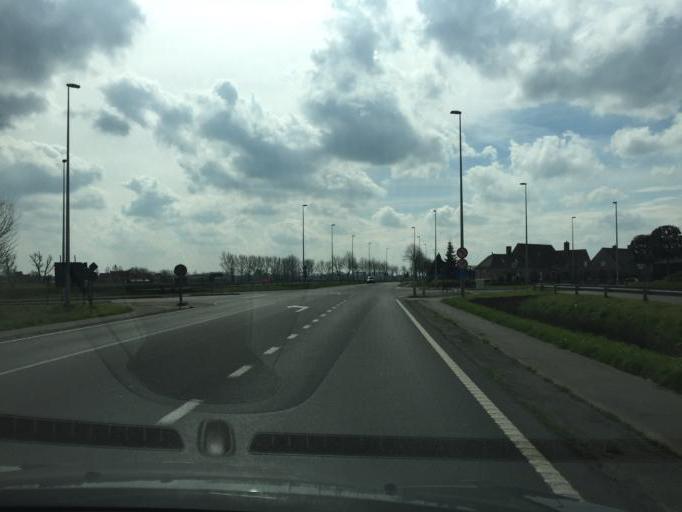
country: BE
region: Flanders
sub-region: Provincie West-Vlaanderen
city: Ruiselede
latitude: 51.0419
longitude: 3.4106
